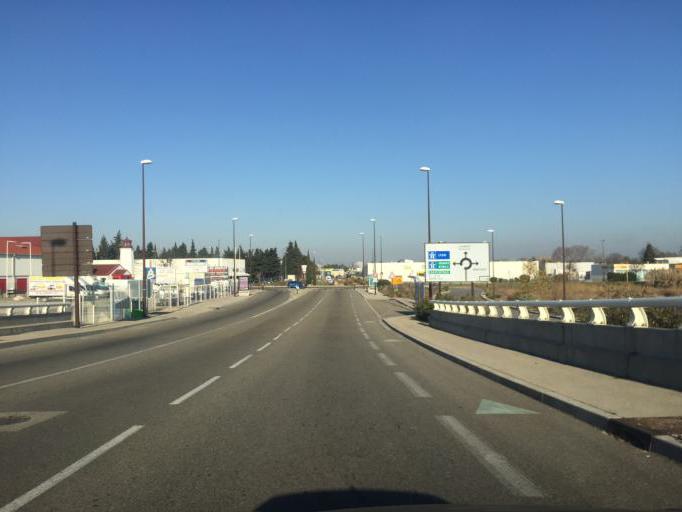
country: FR
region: Provence-Alpes-Cote d'Azur
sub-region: Departement du Vaucluse
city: Montfavet
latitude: 43.9342
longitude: 4.8478
